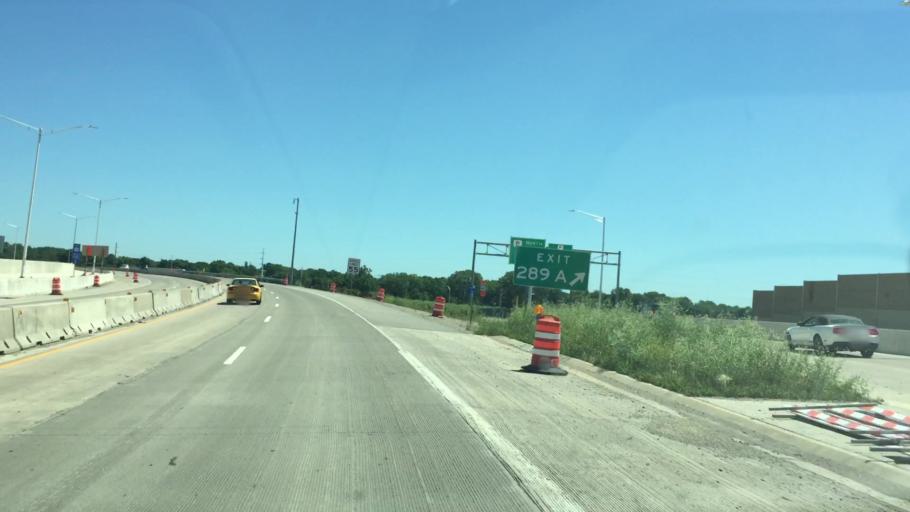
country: US
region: Wisconsin
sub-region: Winnebago County
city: Menasha
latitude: 44.2185
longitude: -88.4521
